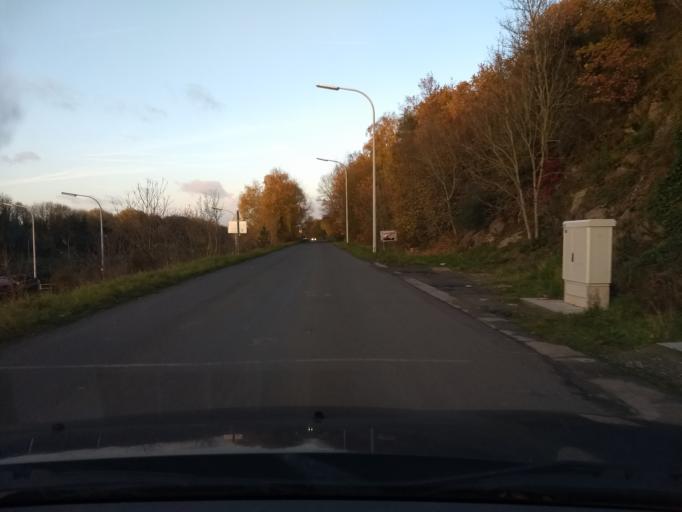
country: BE
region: Wallonia
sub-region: Province du Brabant Wallon
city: Ittre
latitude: 50.6074
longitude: 4.2250
